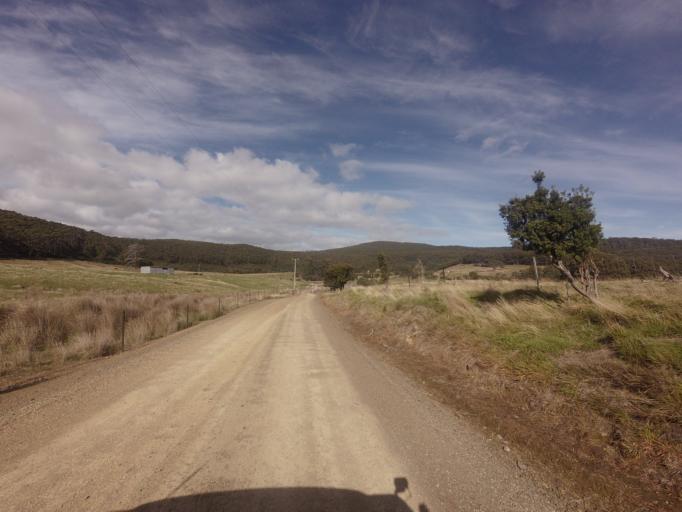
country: AU
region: Tasmania
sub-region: Clarence
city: Sandford
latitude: -43.1889
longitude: 147.7752
